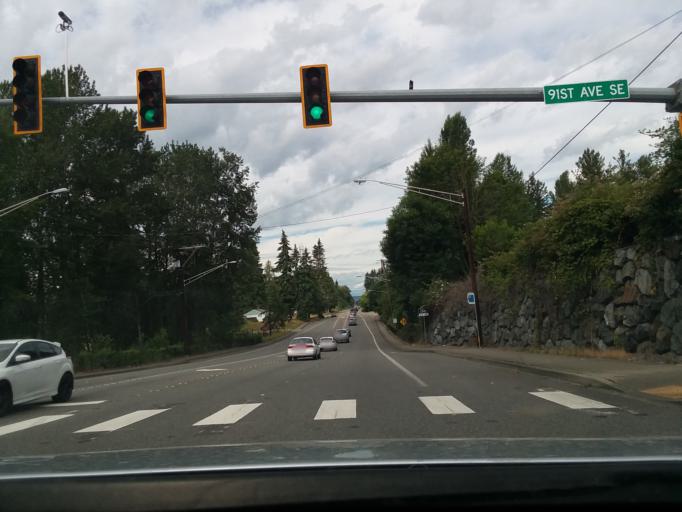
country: US
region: Washington
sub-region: Snohomish County
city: West Lake Stevens
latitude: 47.9781
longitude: -122.1091
